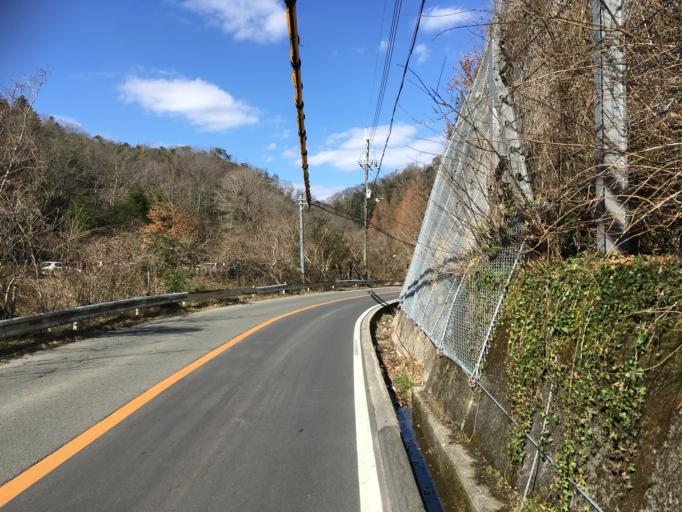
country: JP
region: Osaka
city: Neyagawa
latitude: 34.7543
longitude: 135.6896
